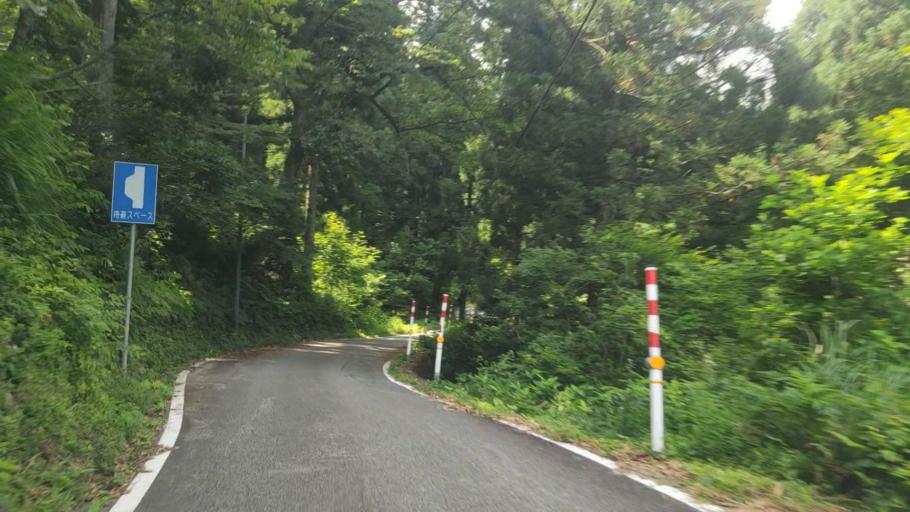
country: JP
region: Fukui
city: Katsuyama
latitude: 36.2115
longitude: 136.5282
